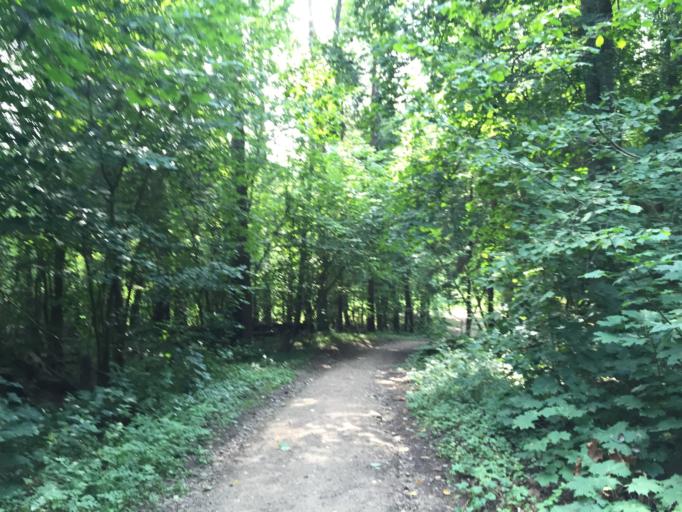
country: LV
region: Dagda
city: Dagda
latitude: 56.2698
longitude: 27.6571
